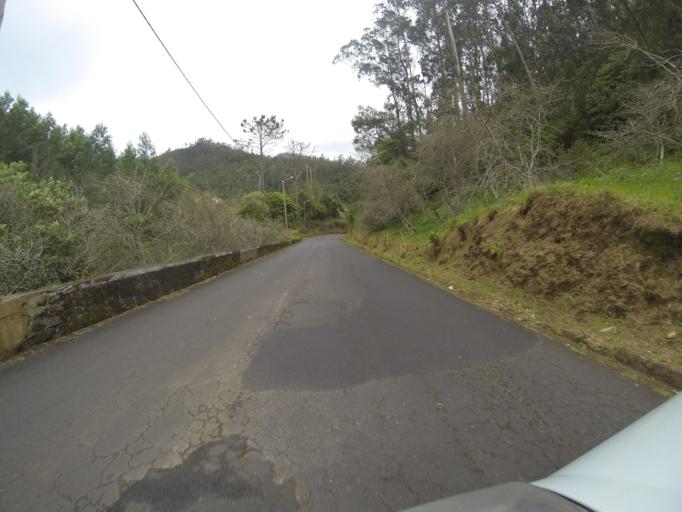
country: PT
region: Madeira
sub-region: Santa Cruz
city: Santa Cruz
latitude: 32.7378
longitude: -16.8208
